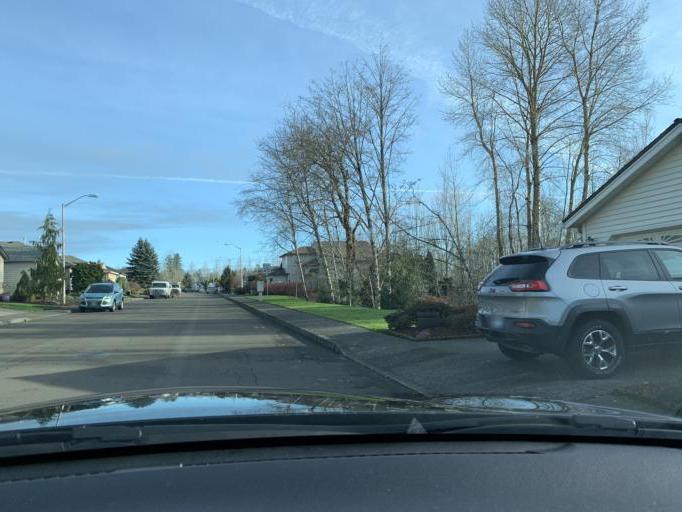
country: US
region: Washington
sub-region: Clark County
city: Mill Plain
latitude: 45.5951
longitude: -122.5116
